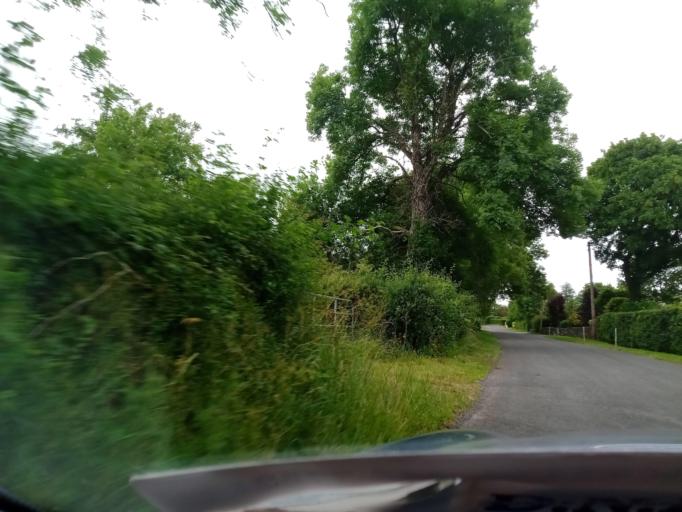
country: IE
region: Leinster
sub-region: Kilkenny
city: Thomastown
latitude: 52.5712
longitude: -7.1954
